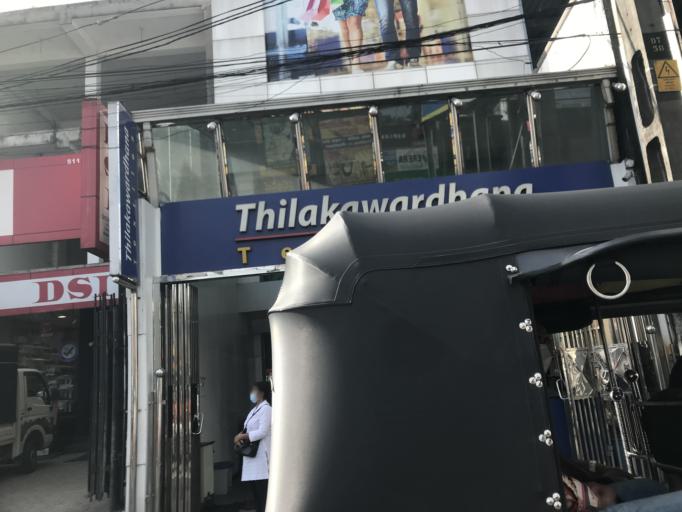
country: LK
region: Western
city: Kelaniya
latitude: 6.9770
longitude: 79.9259
